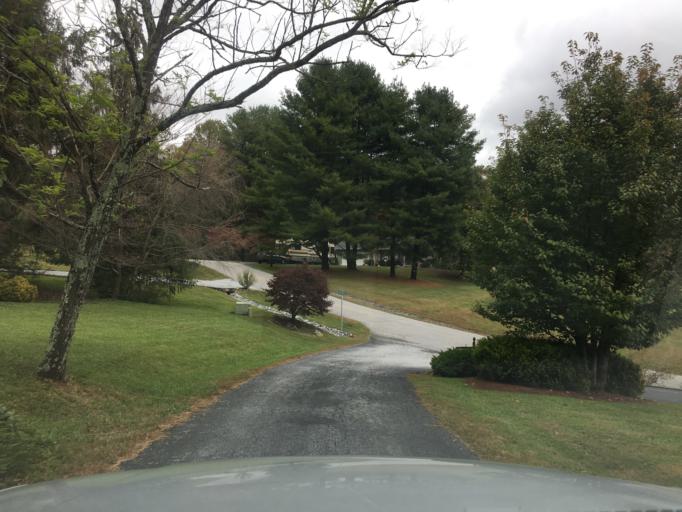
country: US
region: North Carolina
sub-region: Henderson County
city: Laurel Park
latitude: 35.3019
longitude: -82.5076
